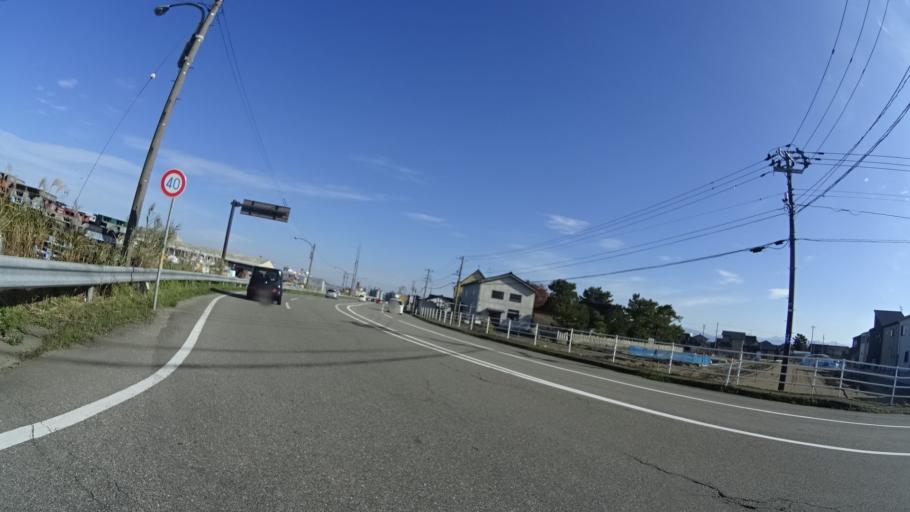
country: JP
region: Ishikawa
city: Kanazawa-shi
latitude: 36.6099
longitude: 136.6071
